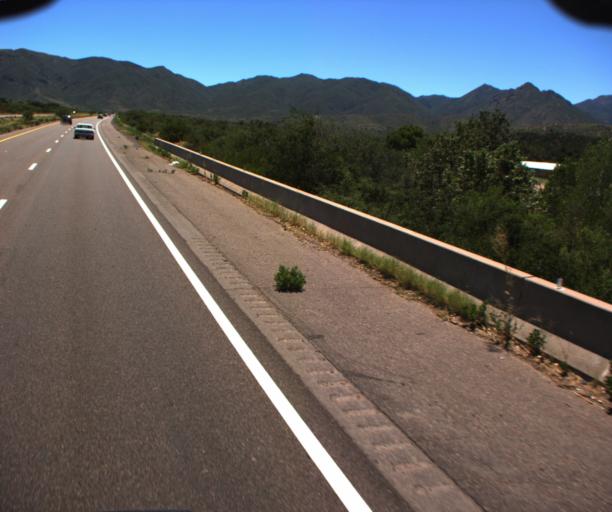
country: US
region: Arizona
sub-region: Gila County
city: Payson
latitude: 34.0582
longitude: -111.3629
